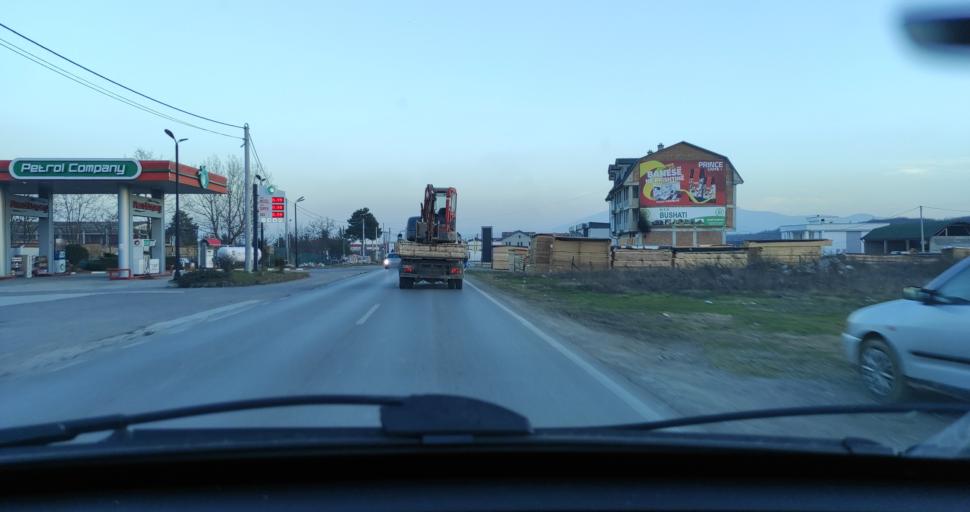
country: XK
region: Gjakova
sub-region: Komuna e Gjakoves
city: Gjakove
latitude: 42.4109
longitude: 20.4032
